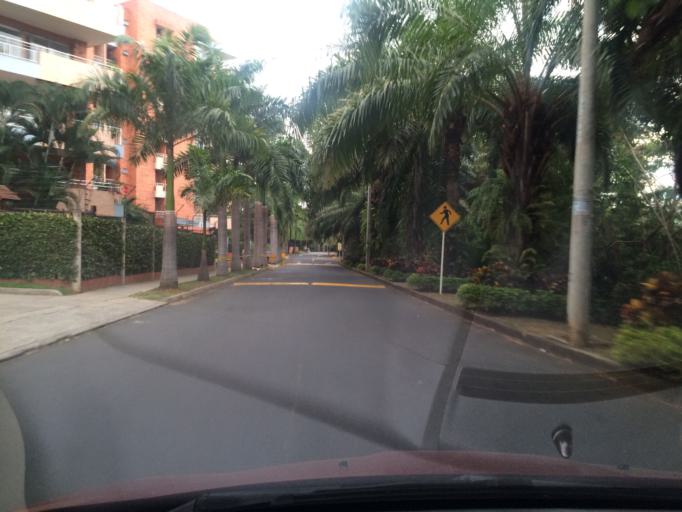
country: CO
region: Valle del Cauca
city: Cali
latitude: 3.3621
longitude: -76.5383
